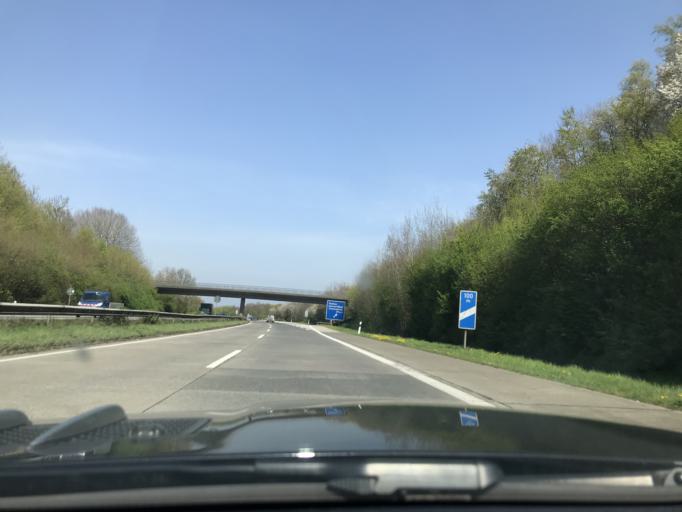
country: DE
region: Schleswig-Holstein
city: Ratekau
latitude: 53.9441
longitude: 10.7463
